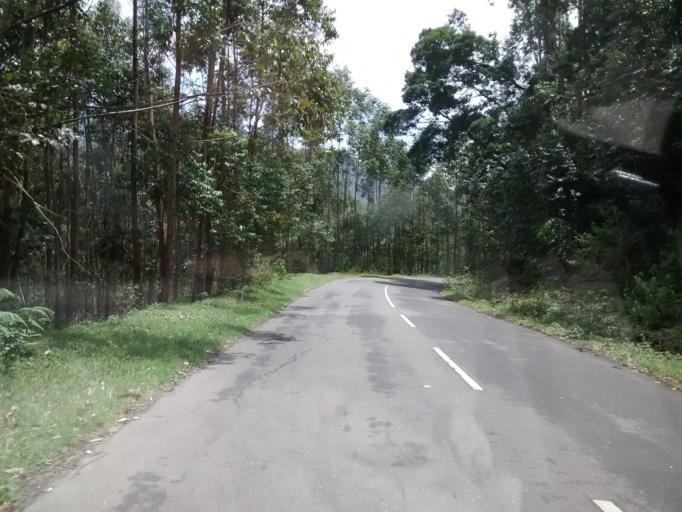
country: IN
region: Kerala
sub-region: Idukki
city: Munnar
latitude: 10.1278
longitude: 77.1637
